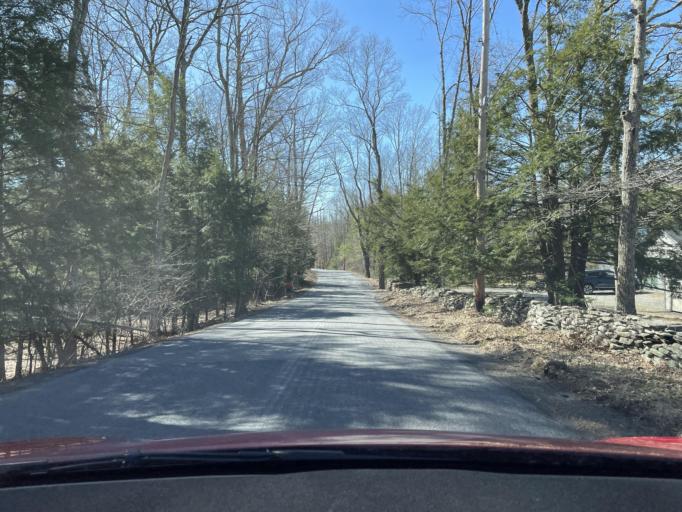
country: US
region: New York
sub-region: Ulster County
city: Zena
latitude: 42.0640
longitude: -74.0264
